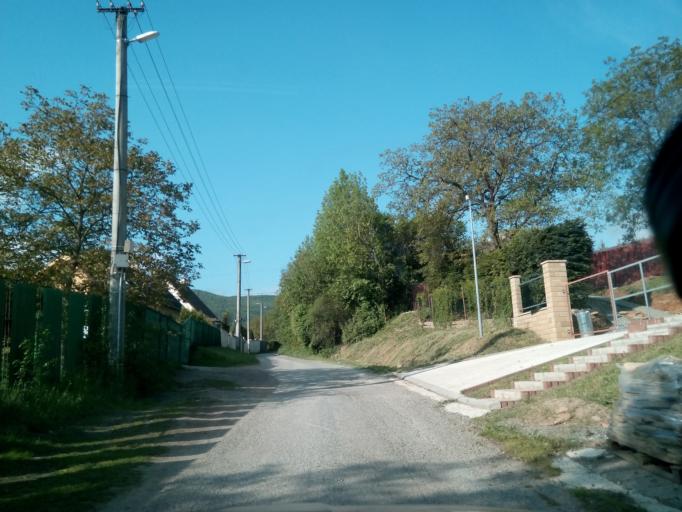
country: SK
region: Kosicky
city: Kosice
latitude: 48.8498
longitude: 21.2176
